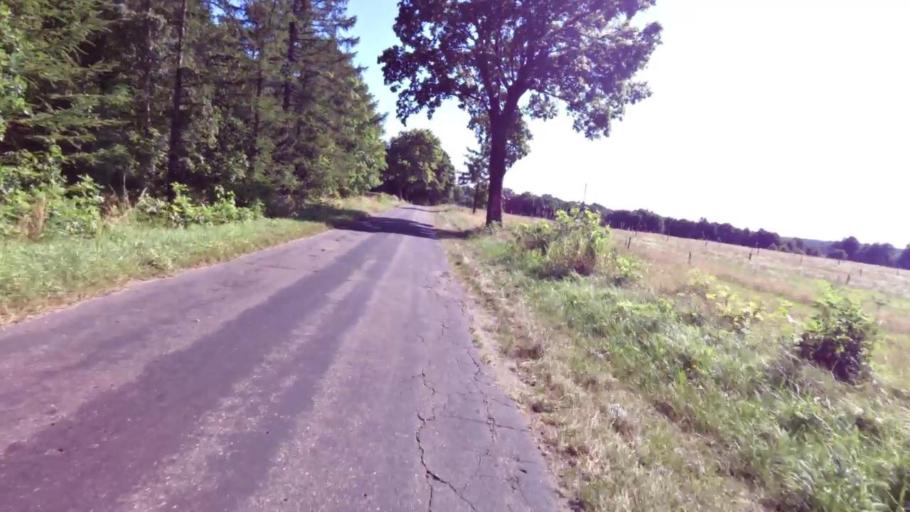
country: PL
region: West Pomeranian Voivodeship
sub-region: Powiat szczecinecki
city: Szczecinek
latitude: 53.7841
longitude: 16.6774
